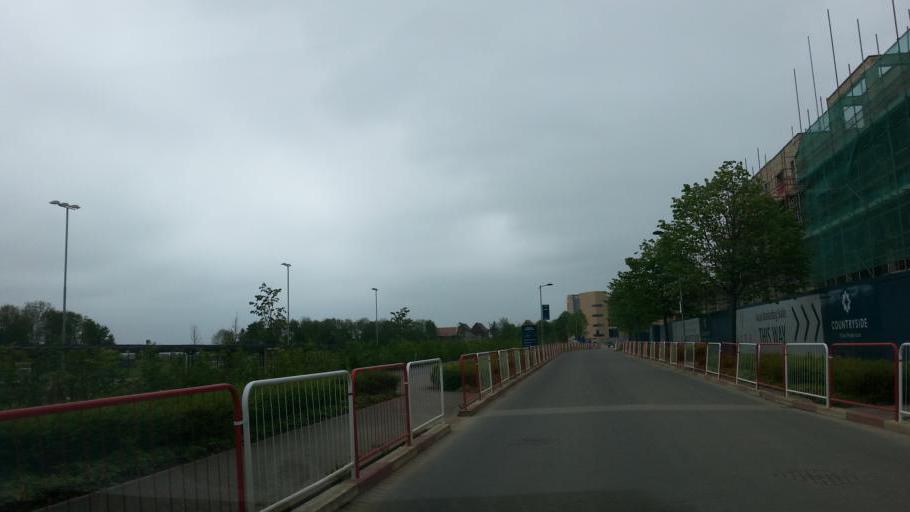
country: GB
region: England
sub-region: Cambridgeshire
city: Cambridge
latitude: 52.1759
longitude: 0.1228
